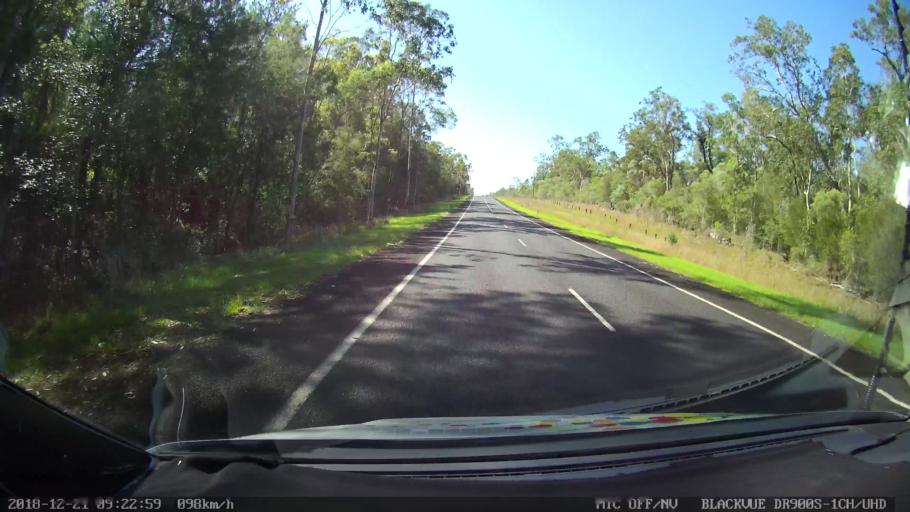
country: AU
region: New South Wales
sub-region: Clarence Valley
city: Maclean
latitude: -29.3487
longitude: 153.0096
